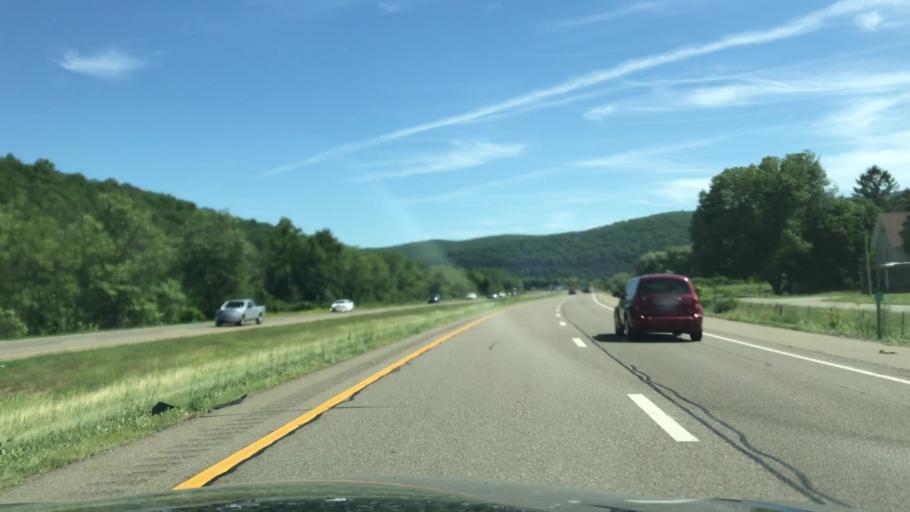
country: US
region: New York
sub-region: Steuben County
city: Gang Mills
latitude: 42.1968
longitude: -77.1617
